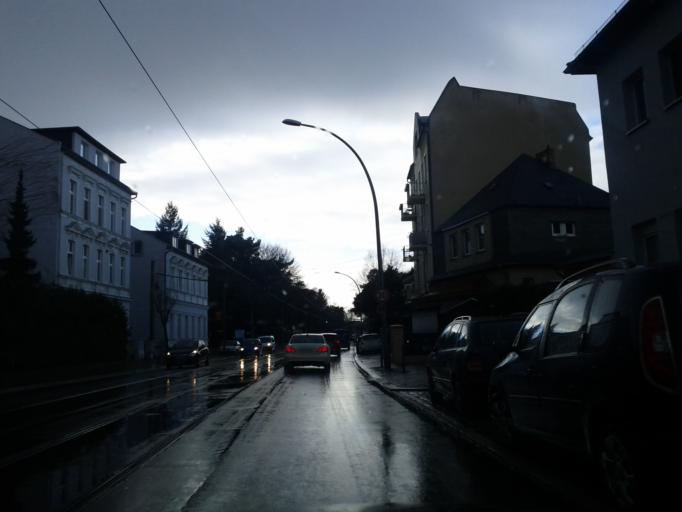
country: DE
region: Berlin
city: Friedrichshagen
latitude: 52.4465
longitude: 13.6181
